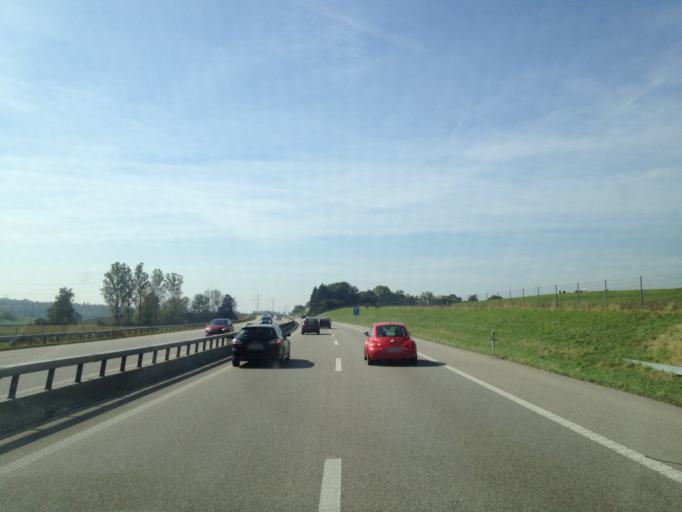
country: CH
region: Bern
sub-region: Oberaargau
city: Oberbipp
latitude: 47.2544
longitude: 7.6768
